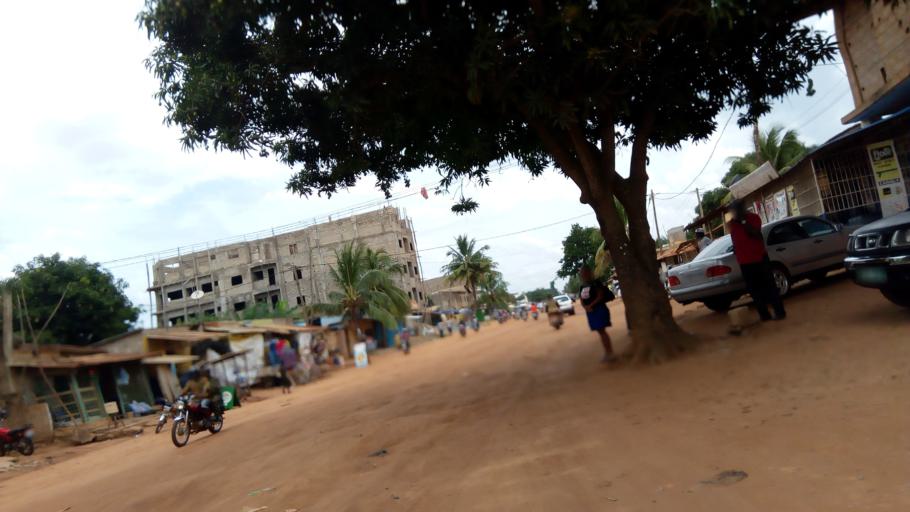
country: TG
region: Maritime
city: Lome
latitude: 6.2190
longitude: 1.1686
